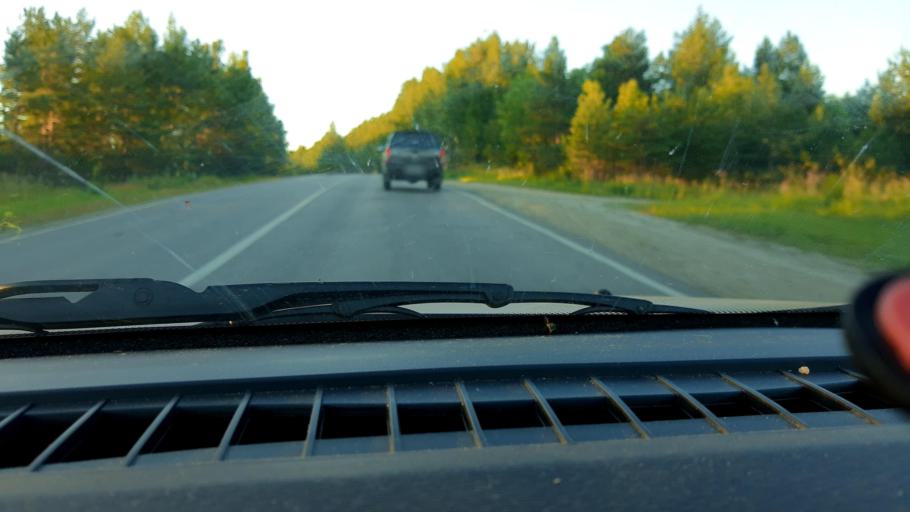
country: RU
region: Nizjnij Novgorod
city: Krasnyye Baki
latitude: 57.0456
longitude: 45.1332
